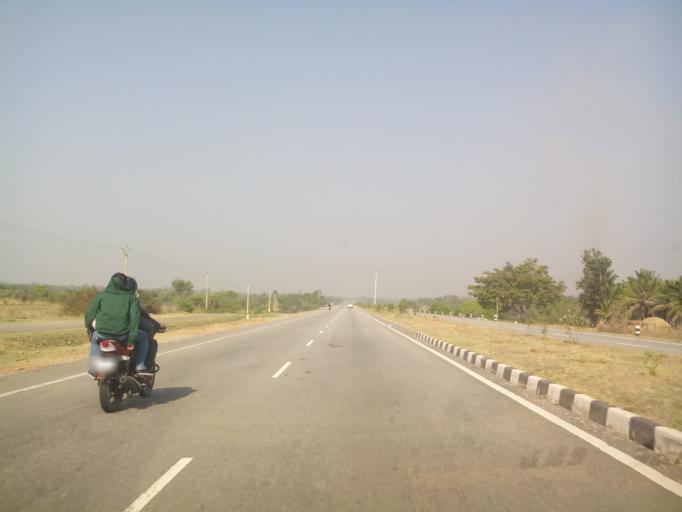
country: IN
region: Karnataka
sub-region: Tumkur
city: Kunigal
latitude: 13.0050
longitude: 77.0096
